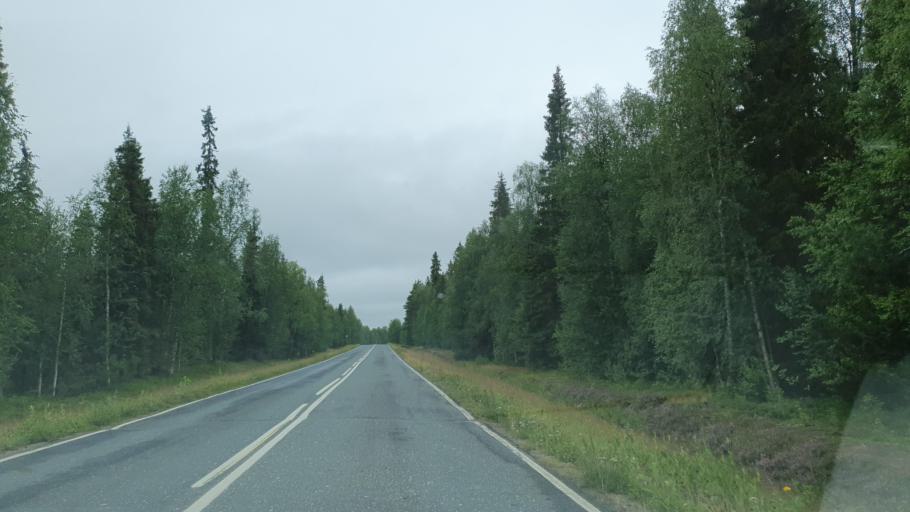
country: FI
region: Lapland
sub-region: Itae-Lappi
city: Pelkosenniemi
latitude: 67.2294
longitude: 27.3490
